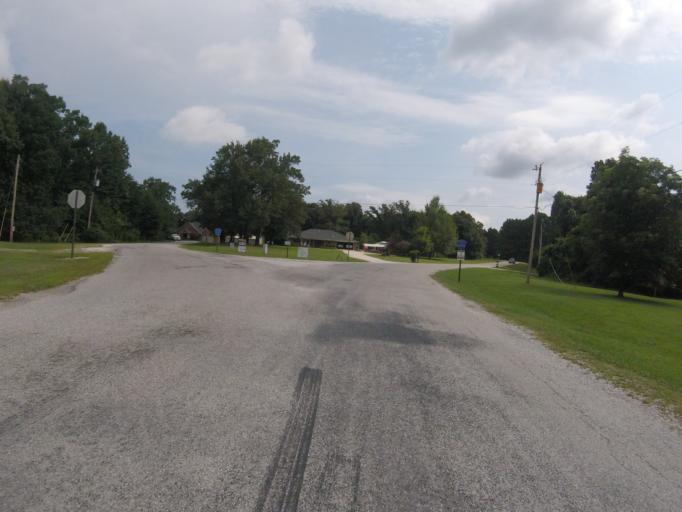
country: US
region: Arkansas
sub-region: Washington County
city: Farmington
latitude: 36.0819
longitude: -94.3004
